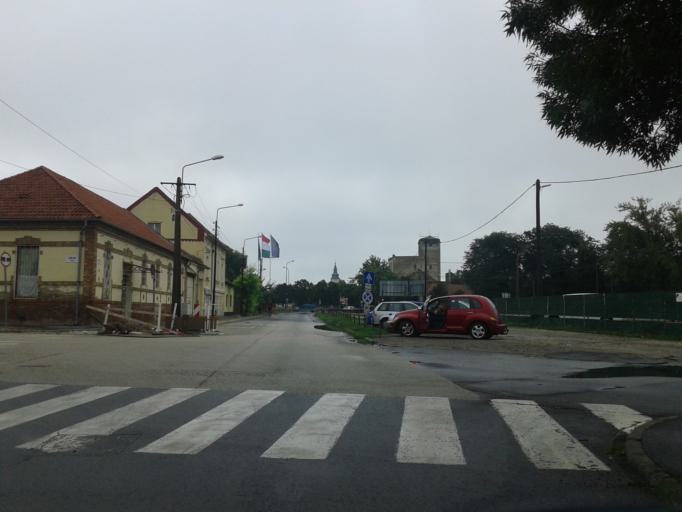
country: HU
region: Csongrad
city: Szeged
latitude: 46.2441
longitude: 20.1287
